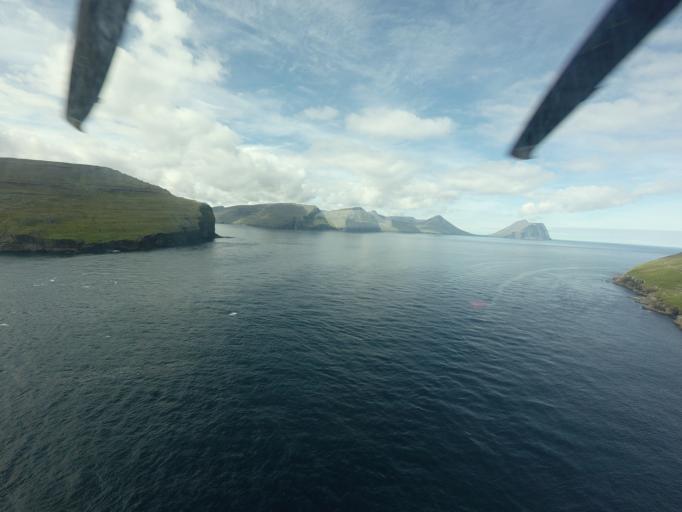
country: FO
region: Nordoyar
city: Klaksvik
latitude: 62.3124
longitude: -6.3067
